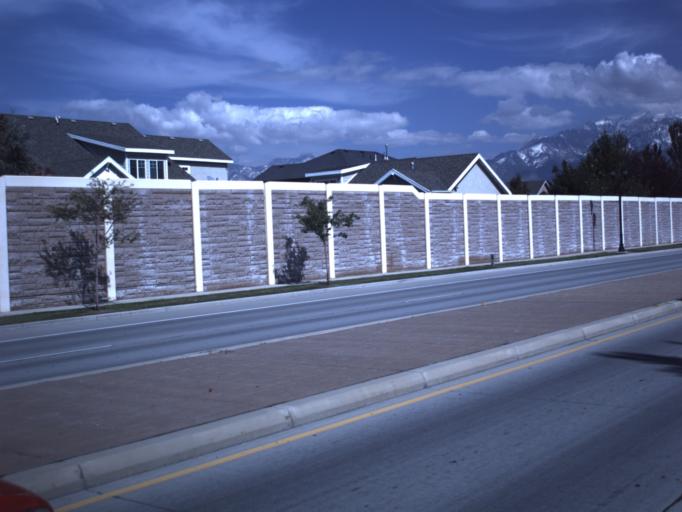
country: US
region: Utah
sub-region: Salt Lake County
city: South Jordan
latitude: 40.5442
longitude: -111.9206
